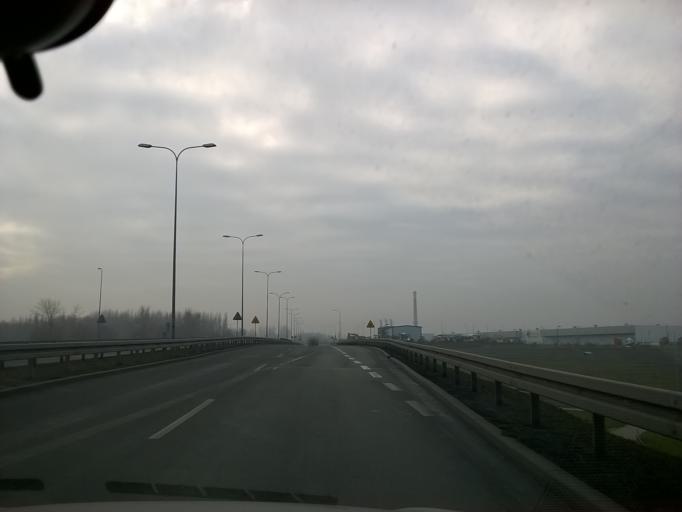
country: PL
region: Silesian Voivodeship
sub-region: Ruda Slaska
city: Ruda Slaska
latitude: 50.2933
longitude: 18.8563
